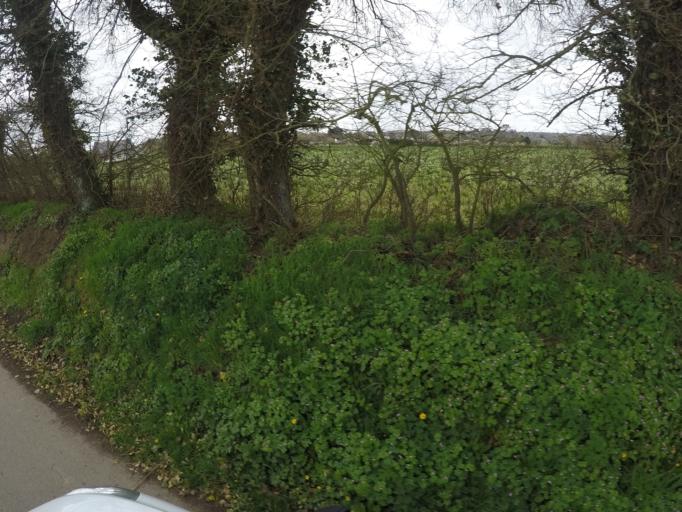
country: FR
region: Brittany
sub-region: Departement des Cotes-d'Armor
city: Plouezec
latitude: 48.7167
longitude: -2.9582
